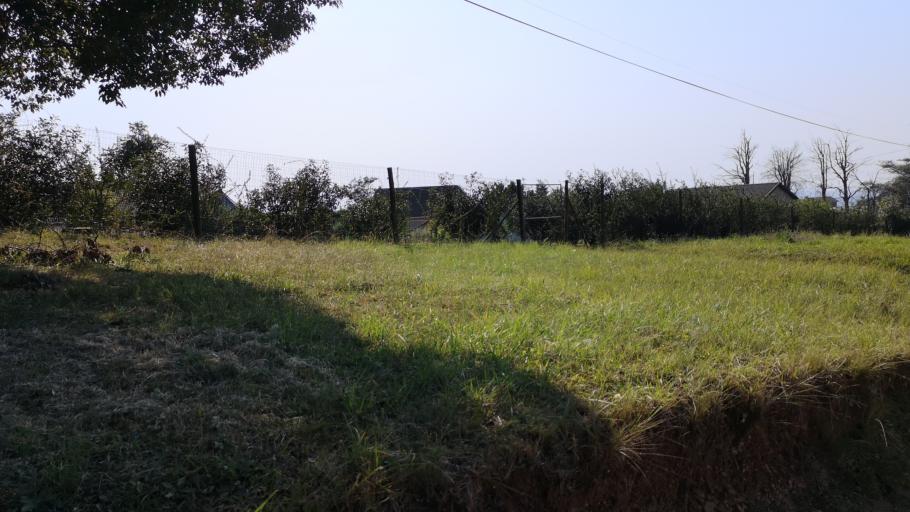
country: ZA
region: KwaZulu-Natal
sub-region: eThekwini Metropolitan Municipality
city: Mpumalanga
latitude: -29.7367
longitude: 30.6830
